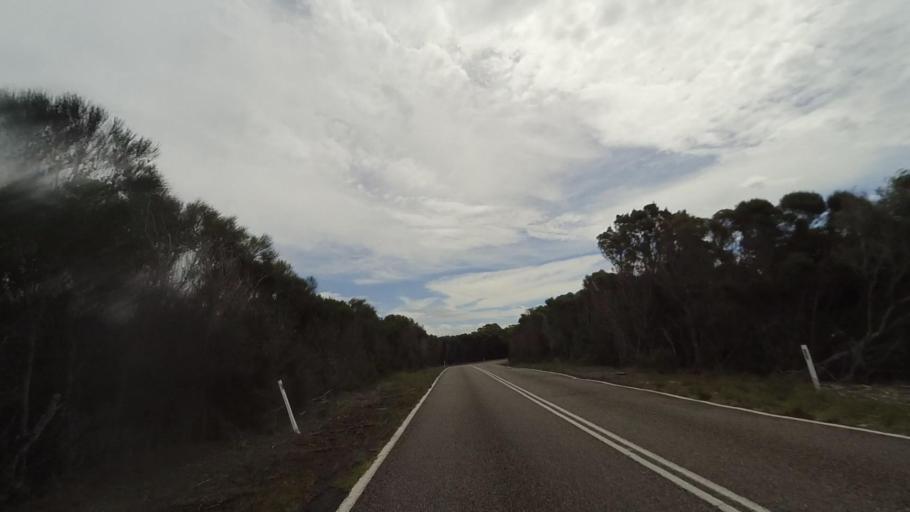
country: AU
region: New South Wales
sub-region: Sutherland Shire
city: Dolans Bay
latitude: -34.1037
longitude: 151.1126
